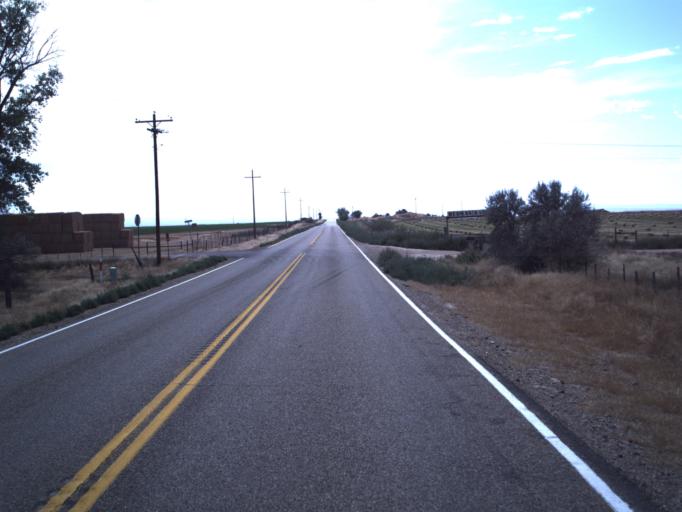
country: US
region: Utah
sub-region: Uintah County
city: Maeser
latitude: 40.2331
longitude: -109.6844
